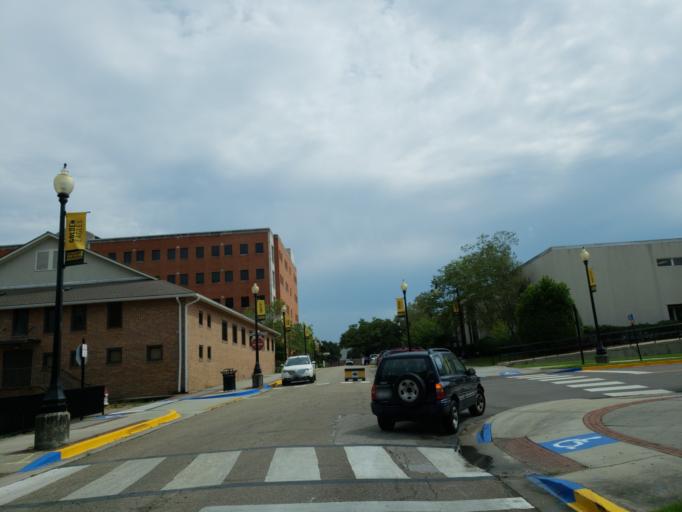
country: US
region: Mississippi
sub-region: Lamar County
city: Arnold Line
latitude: 31.3287
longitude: -89.3348
